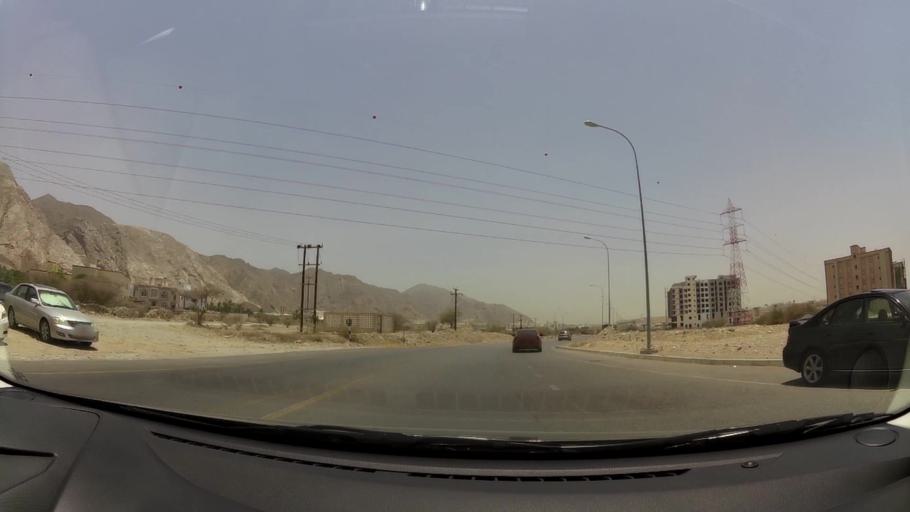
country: OM
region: Muhafazat Masqat
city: Bawshar
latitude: 23.5559
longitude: 58.4102
